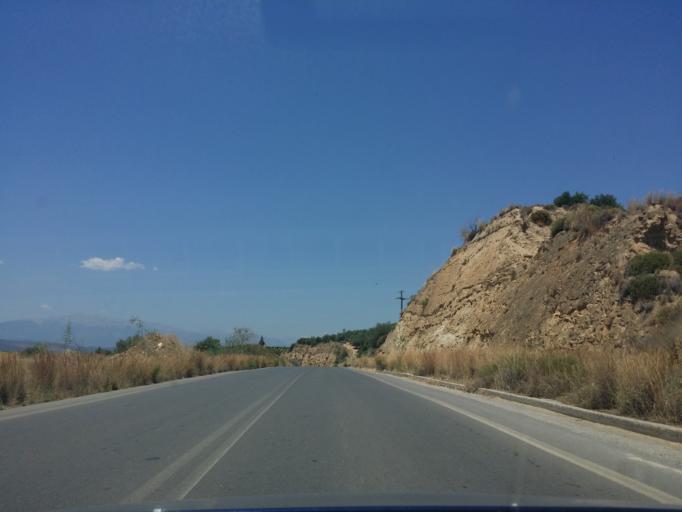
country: GR
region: Peloponnese
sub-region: Nomos Lakonias
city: Vlakhiotis
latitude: 36.8588
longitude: 22.7353
